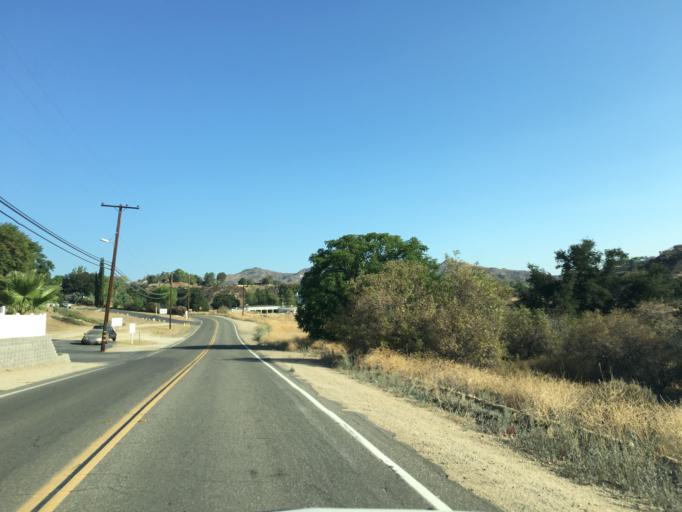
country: US
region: California
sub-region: Los Angeles County
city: Val Verde
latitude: 34.4624
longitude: -118.6597
